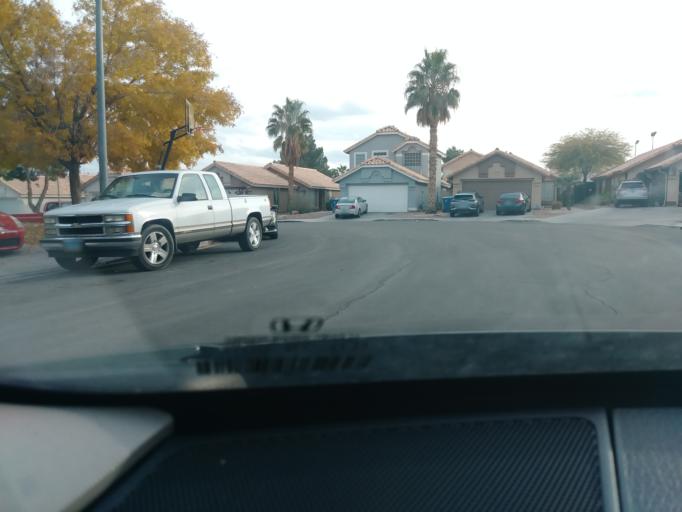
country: US
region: Nevada
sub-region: Clark County
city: Spring Valley
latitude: 36.1798
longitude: -115.2167
